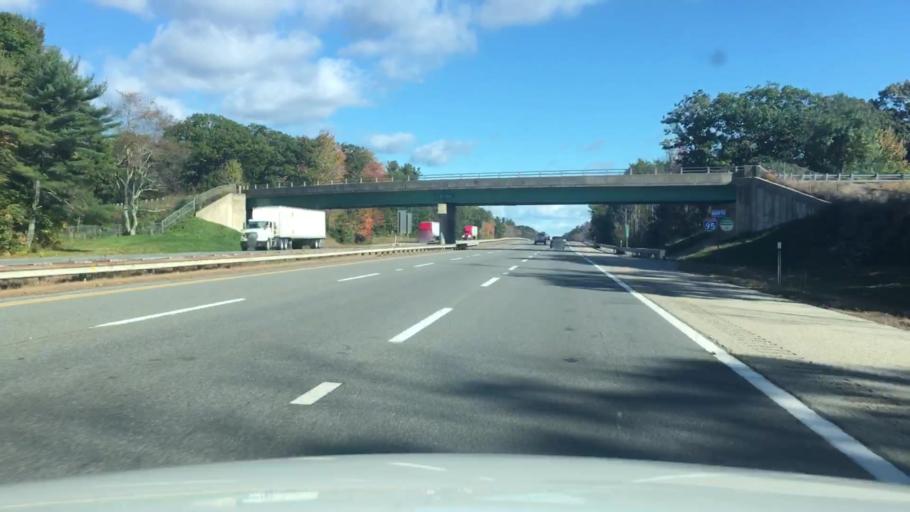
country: US
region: Maine
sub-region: York County
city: Wells Beach Station
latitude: 43.3330
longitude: -70.6026
